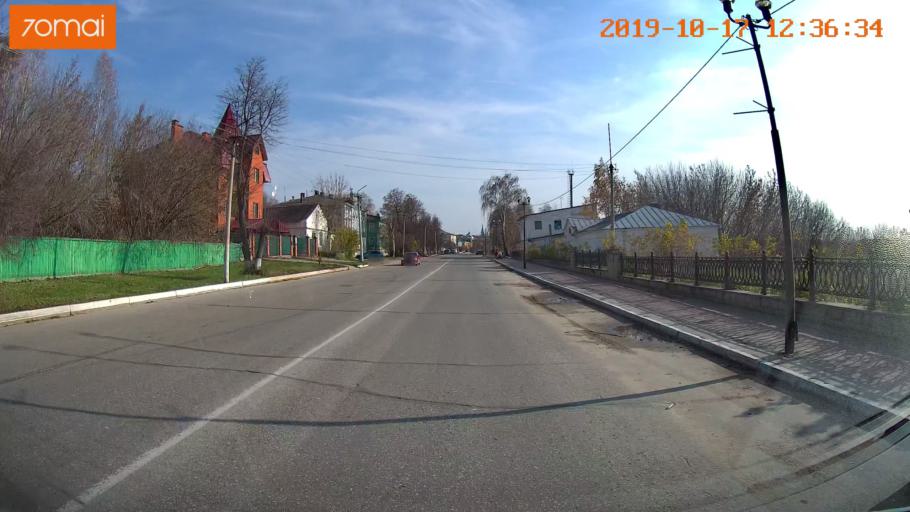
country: RU
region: Rjazan
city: Kasimov
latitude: 54.9395
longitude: 41.3772
